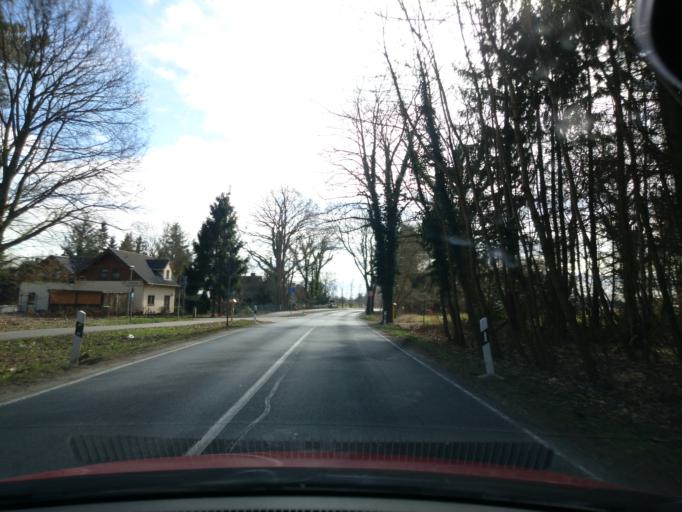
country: DE
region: Mecklenburg-Vorpommern
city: Ostseebad Prerow
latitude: 54.4176
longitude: 12.5774
